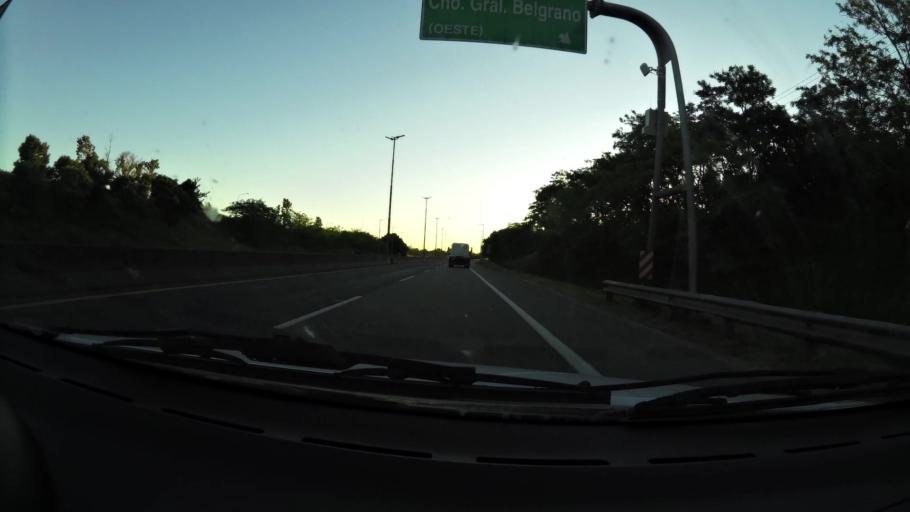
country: AR
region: Buenos Aires
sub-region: Partido de Quilmes
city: Quilmes
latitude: -34.8181
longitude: -58.1851
